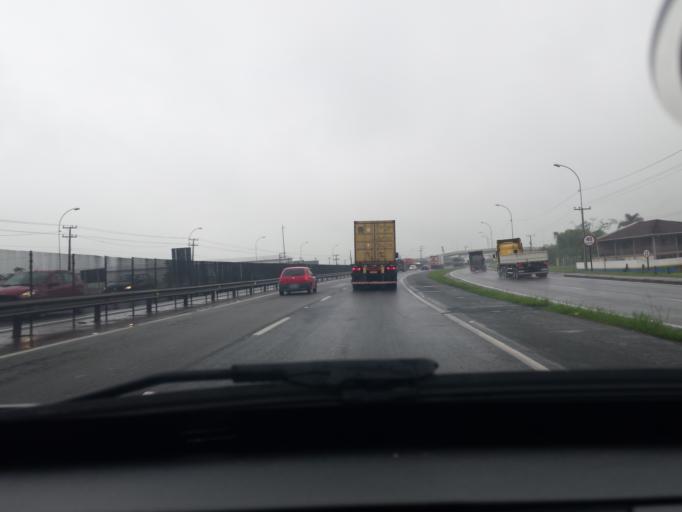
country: BR
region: Santa Catarina
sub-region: Itajai
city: Itajai
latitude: -26.8515
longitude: -48.7262
